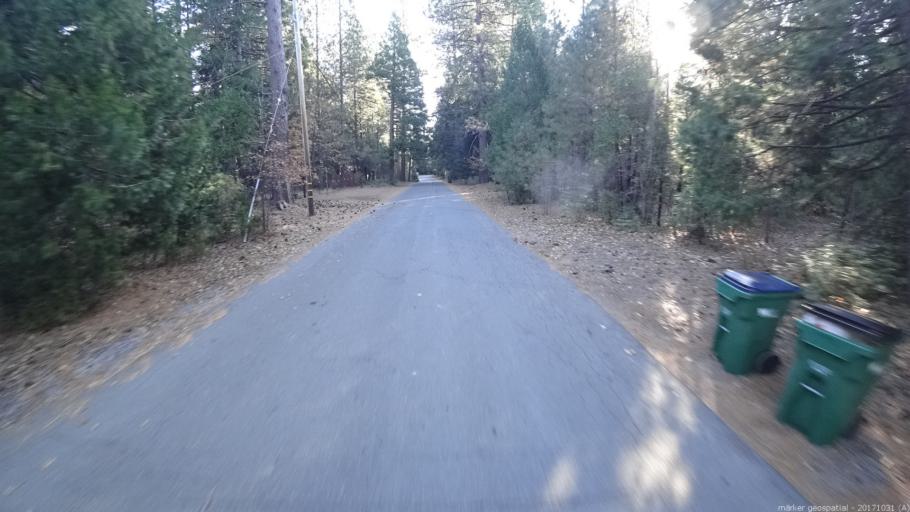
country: US
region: California
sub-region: Shasta County
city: Shingletown
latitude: 40.5279
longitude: -121.7491
